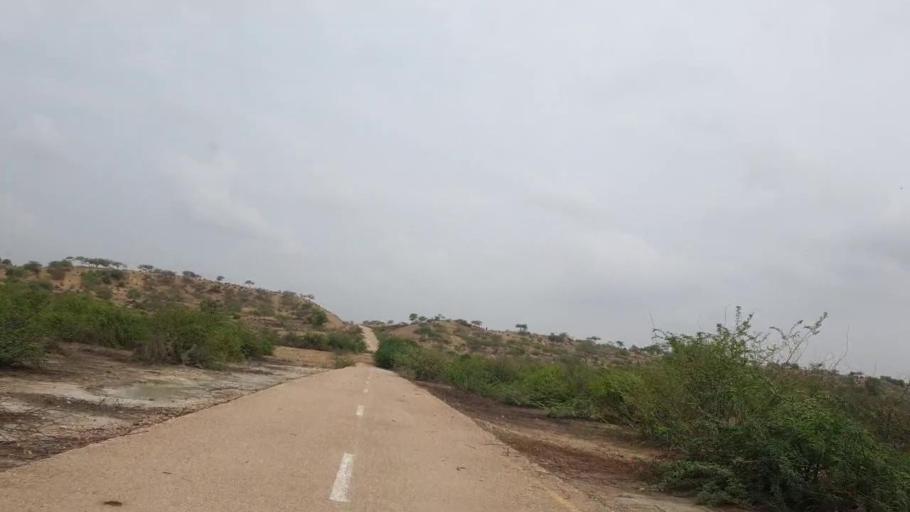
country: PK
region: Sindh
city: Naukot
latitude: 24.6289
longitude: 69.3560
